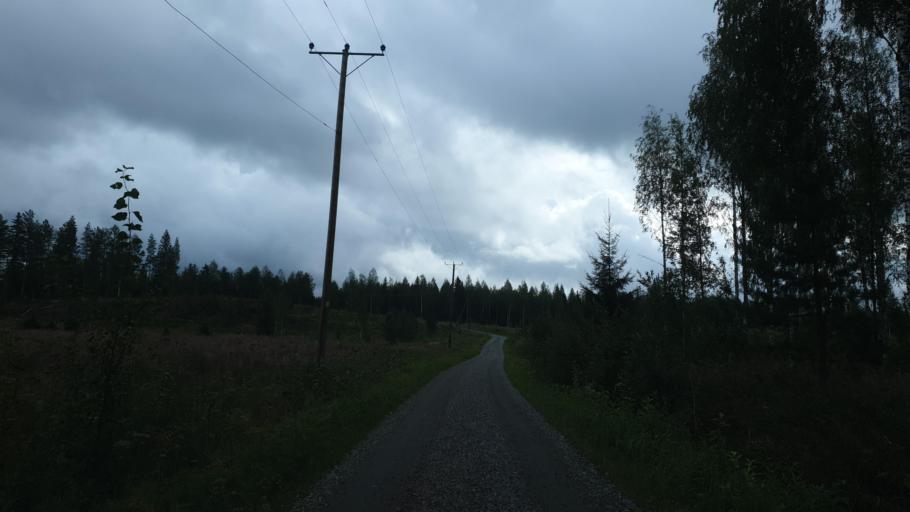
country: FI
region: Northern Savo
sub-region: Kuopio
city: Nilsiae
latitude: 63.2487
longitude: 28.2477
